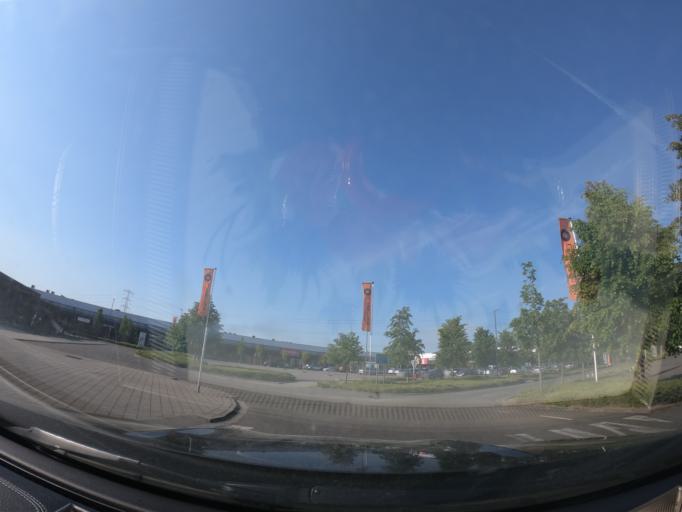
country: BE
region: Flanders
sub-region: Provincie Antwerpen
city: Olen
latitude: 51.1515
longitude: 4.9018
